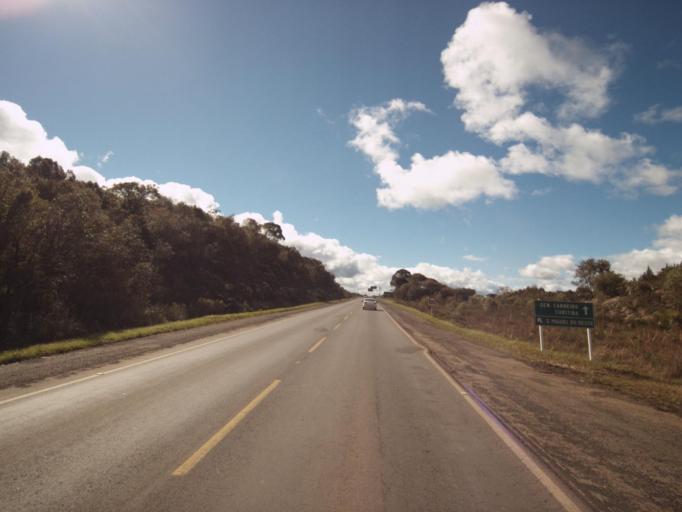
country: BR
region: Santa Catarina
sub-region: Concordia
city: Concordia
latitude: -26.9744
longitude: -51.8596
